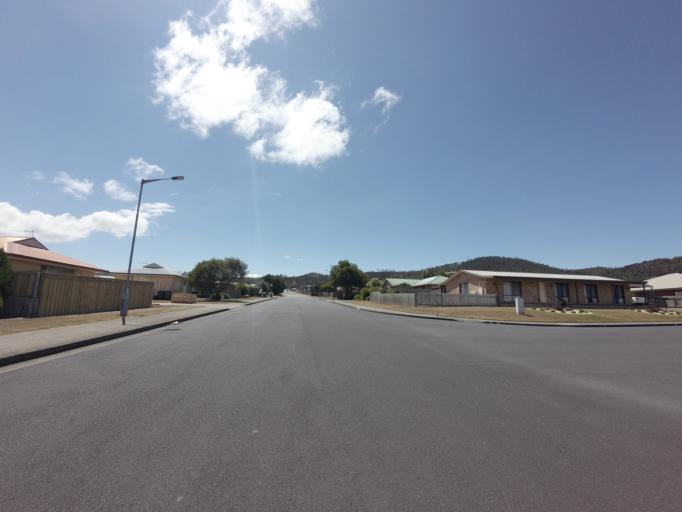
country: AU
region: Tasmania
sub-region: Clarence
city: Rokeby
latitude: -42.9020
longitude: 147.4511
